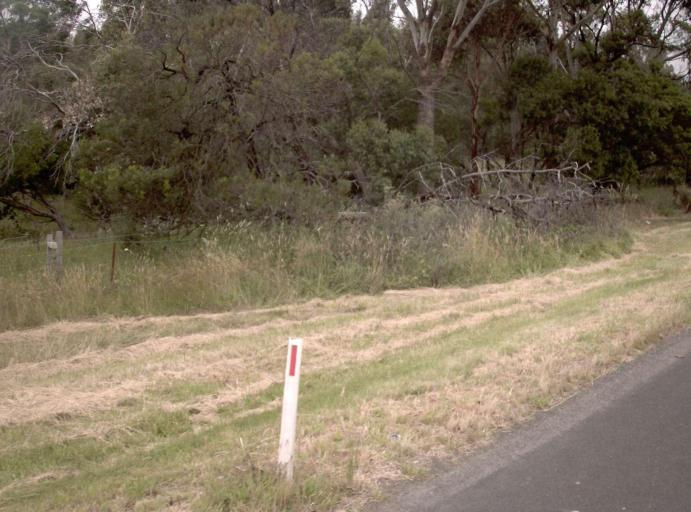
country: AU
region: Victoria
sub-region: Latrobe
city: Morwell
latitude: -38.2713
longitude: 146.4229
